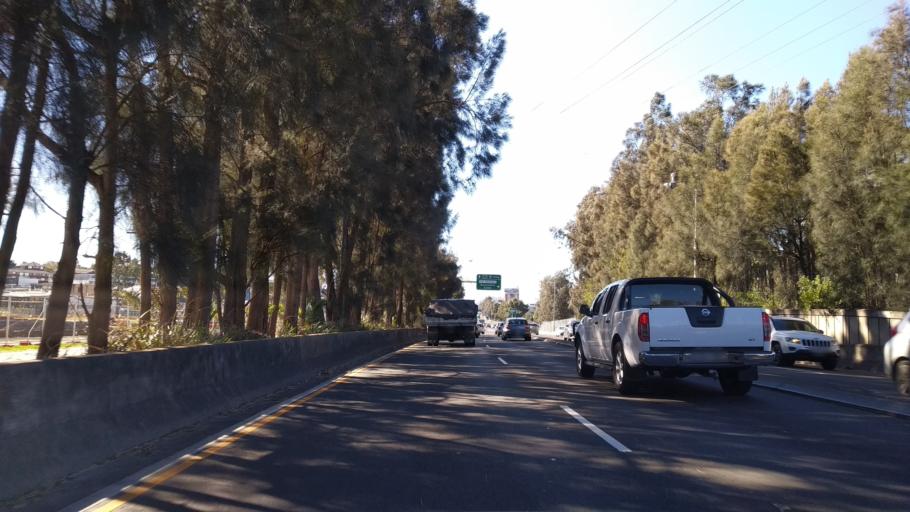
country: AU
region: New South Wales
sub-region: Leichhardt
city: Lilyfield
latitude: -33.8721
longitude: 151.1710
